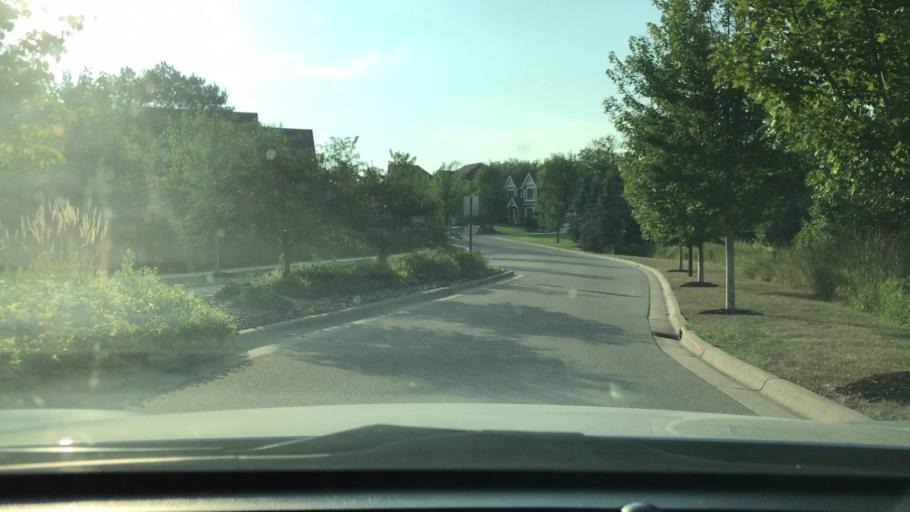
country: US
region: Minnesota
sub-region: Hennepin County
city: Maple Grove
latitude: 45.0533
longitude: -93.4759
